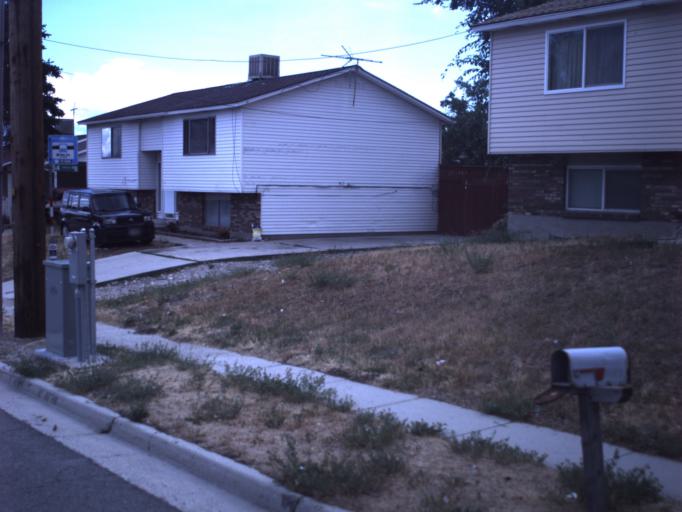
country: US
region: Utah
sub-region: Salt Lake County
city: Kearns
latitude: 40.6530
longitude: -112.0113
